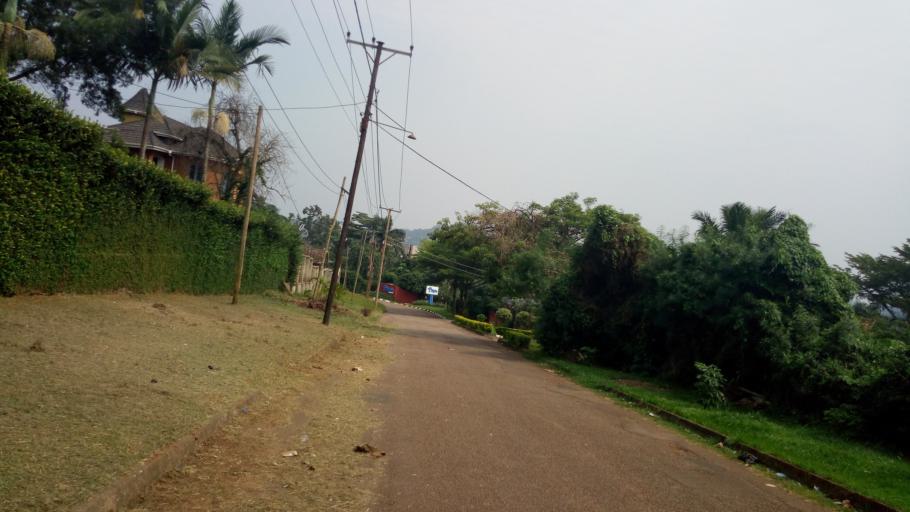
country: UG
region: Central Region
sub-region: Kampala District
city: Kampala
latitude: 0.3129
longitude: 32.6198
